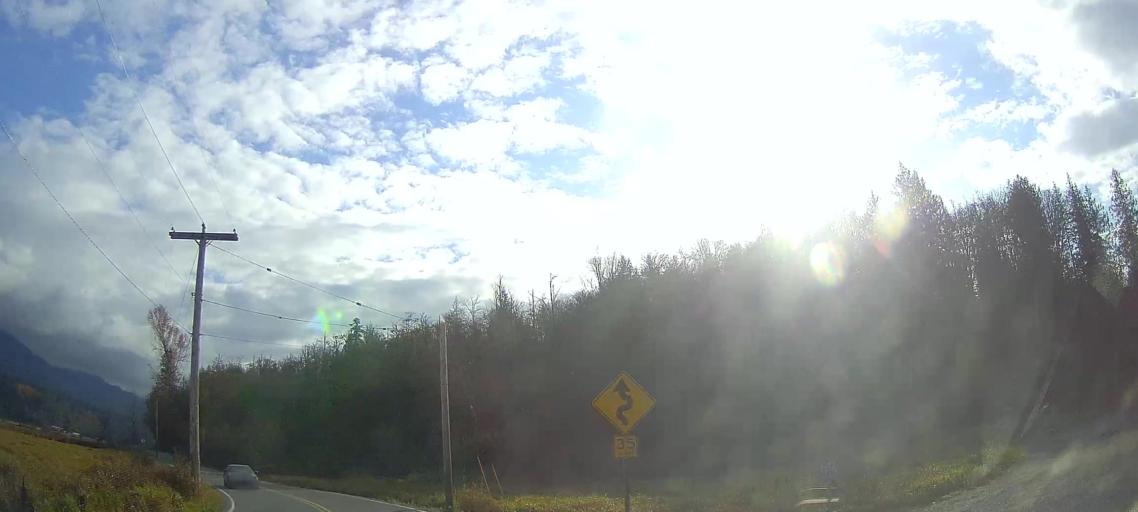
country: US
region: Washington
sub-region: Skagit County
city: Clear Lake
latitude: 48.4497
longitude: -122.2258
